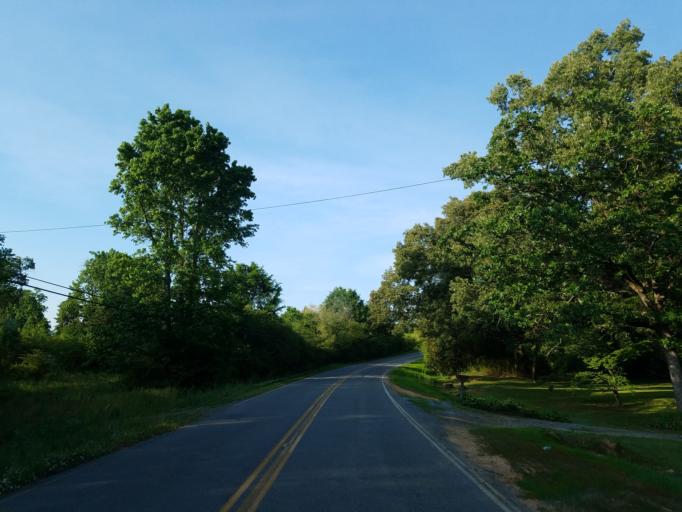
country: US
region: Georgia
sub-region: Floyd County
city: Shannon
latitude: 34.4865
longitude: -85.1332
